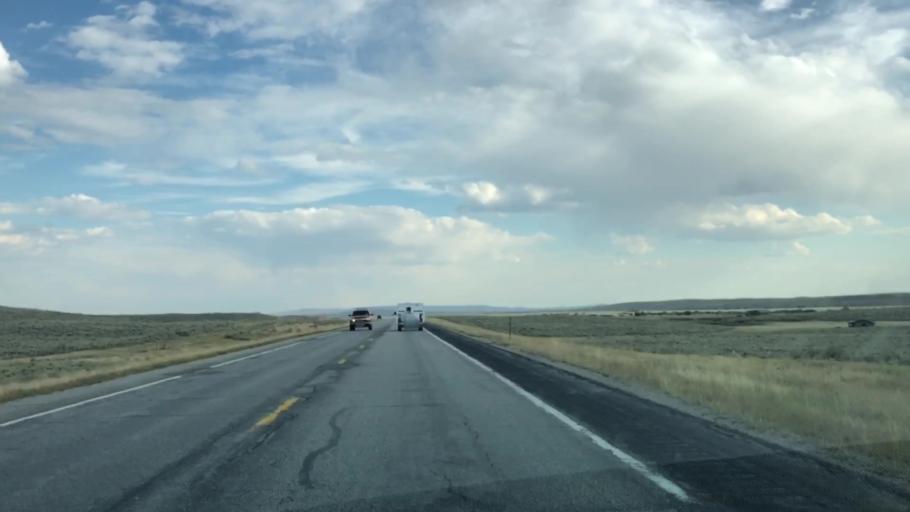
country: US
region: Wyoming
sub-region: Sublette County
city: Pinedale
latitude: 43.0509
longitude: -110.1516
